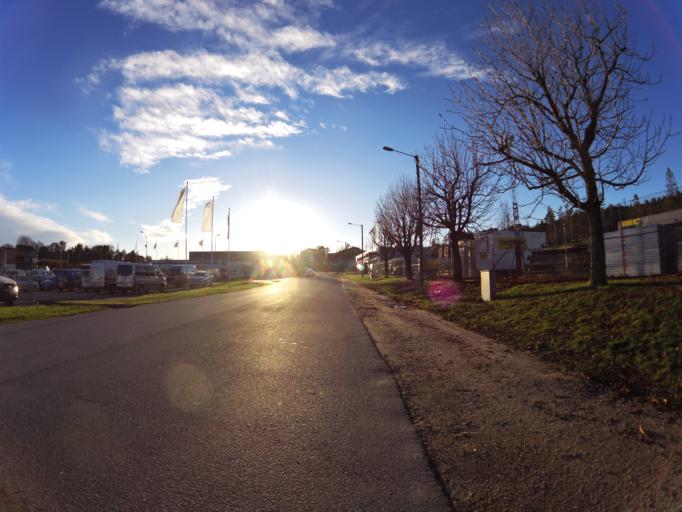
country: NO
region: Ostfold
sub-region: Fredrikstad
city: Fredrikstad
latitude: 59.2387
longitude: 10.9658
